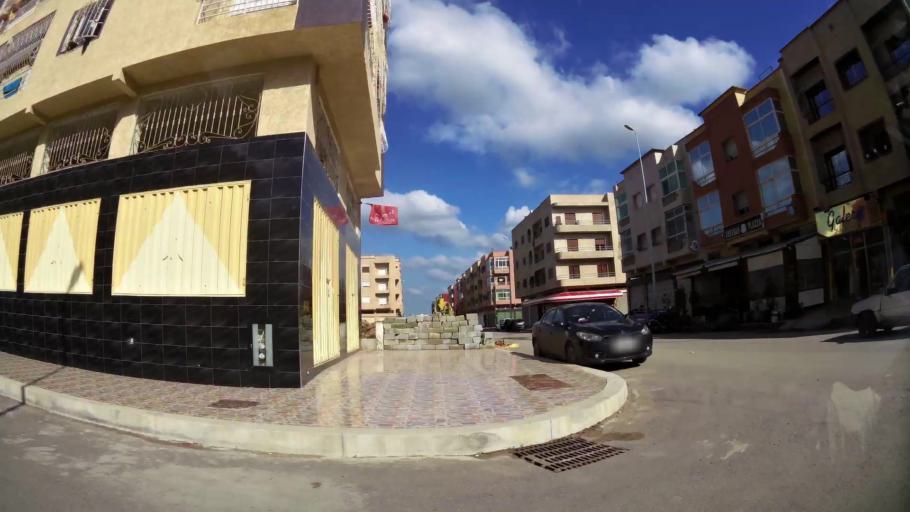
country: MA
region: Grand Casablanca
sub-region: Mediouna
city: Mediouna
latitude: 33.3864
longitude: -7.5306
